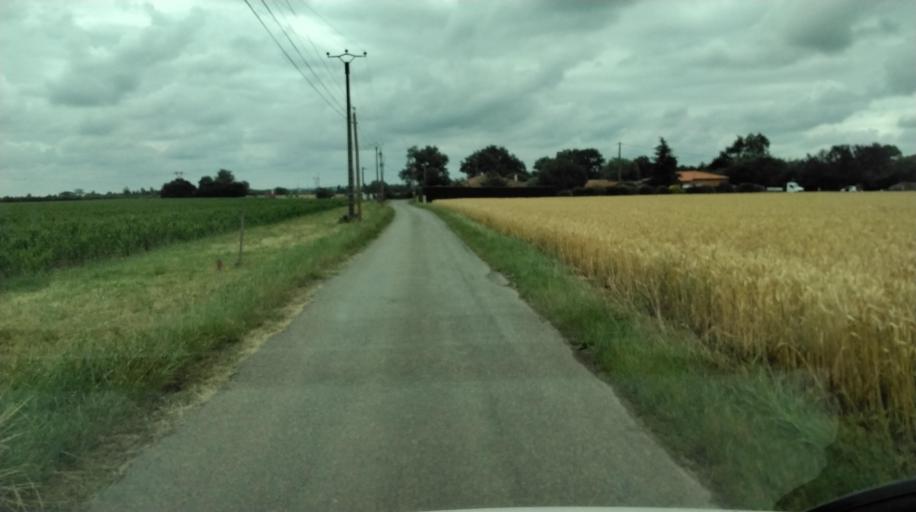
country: FR
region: Midi-Pyrenees
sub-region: Departement de la Haute-Garonne
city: Martres-Tolosane
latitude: 43.2029
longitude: 1.0262
